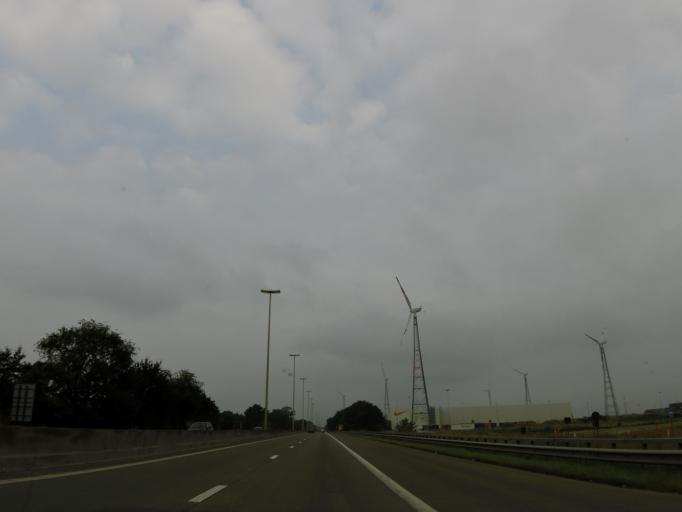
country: BE
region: Flanders
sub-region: Provincie Limburg
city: Tessenderlo
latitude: 51.0930
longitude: 5.1036
